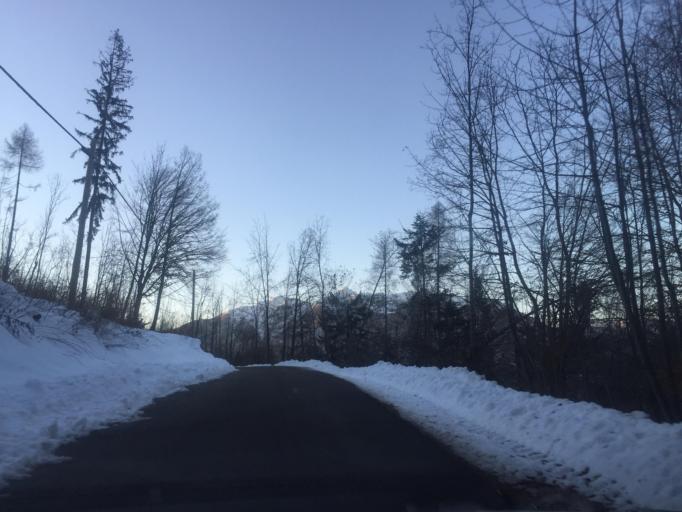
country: IT
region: Friuli Venezia Giulia
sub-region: Provincia di Udine
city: Lauco
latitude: 46.4295
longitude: 12.9422
